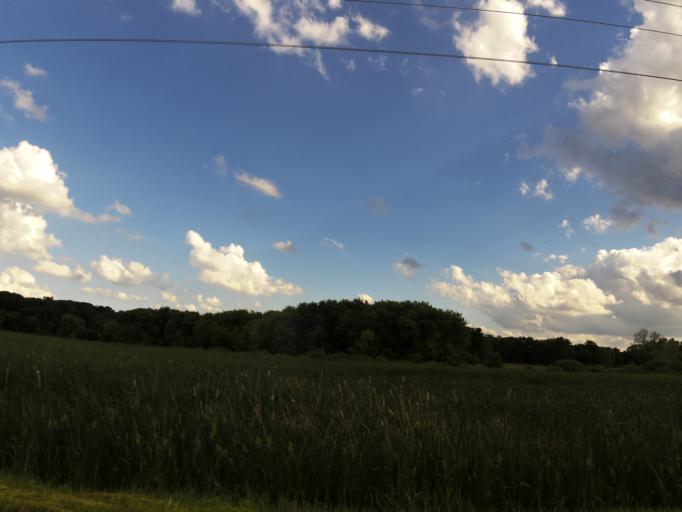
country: US
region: Minnesota
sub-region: Scott County
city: Prior Lake
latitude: 44.6884
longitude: -93.4583
